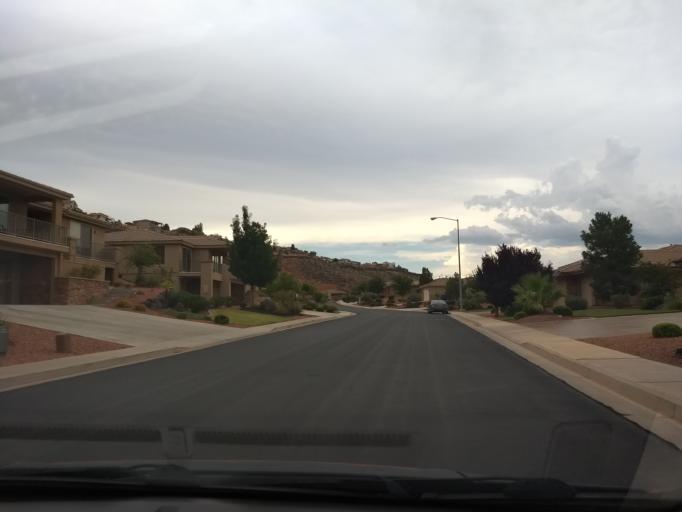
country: US
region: Utah
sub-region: Washington County
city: Saint George
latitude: 37.1067
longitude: -113.5456
